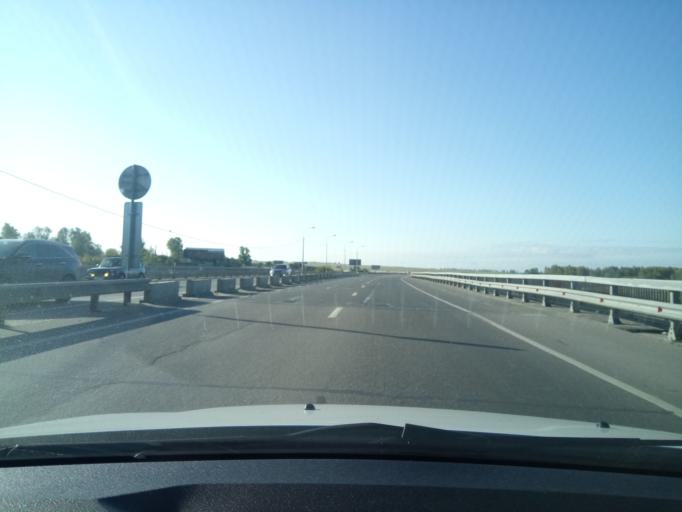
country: RU
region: Nizjnij Novgorod
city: Burevestnik
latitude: 56.1565
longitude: 43.9104
